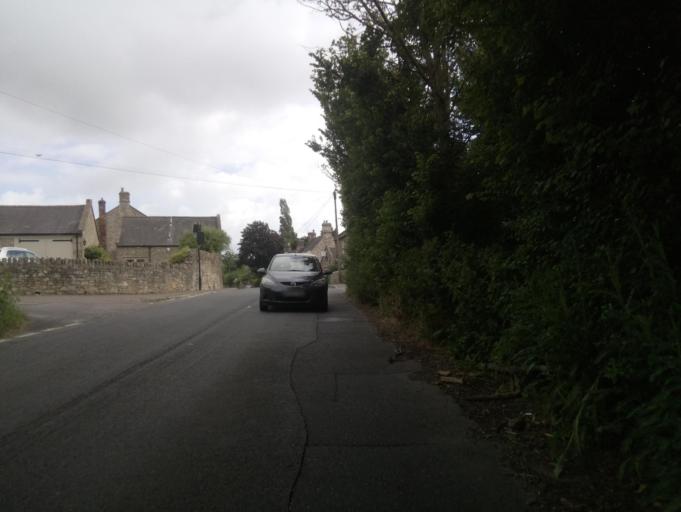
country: GB
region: England
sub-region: Bath and North East Somerset
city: Corston
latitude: 51.4043
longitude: -2.4326
